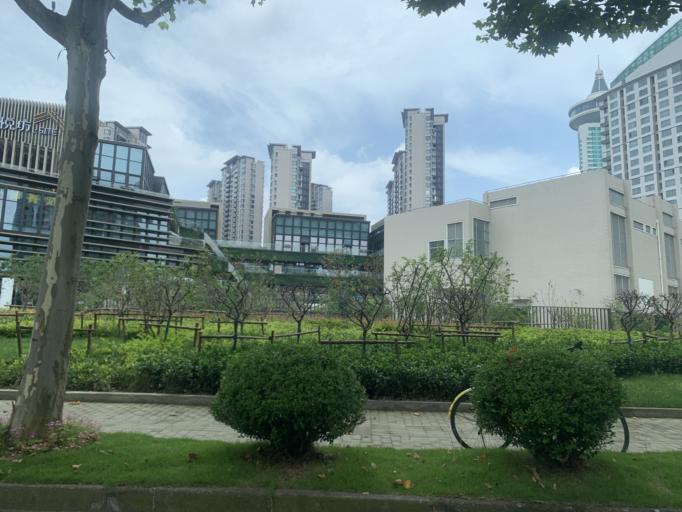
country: CN
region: Shanghai Shi
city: Huamu
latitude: 31.2108
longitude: 121.5329
